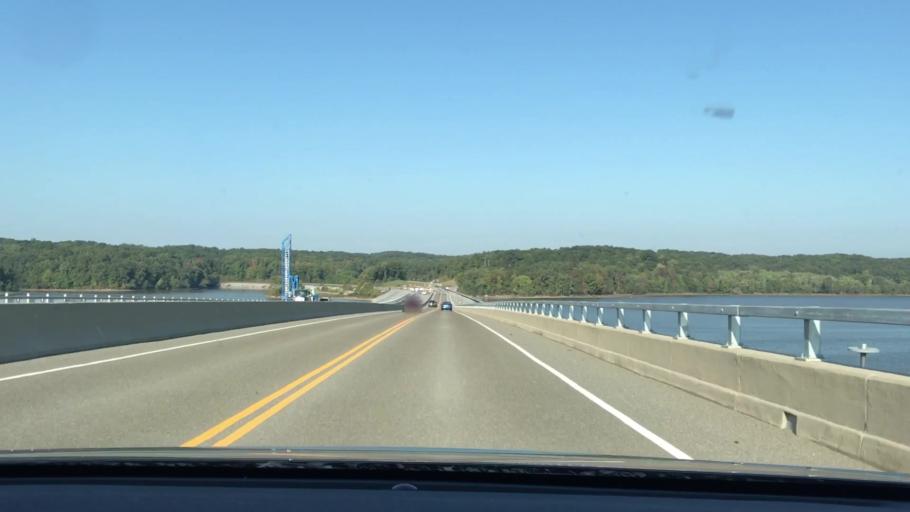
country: US
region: Kentucky
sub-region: Trigg County
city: Cadiz
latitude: 36.8003
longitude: -87.9775
